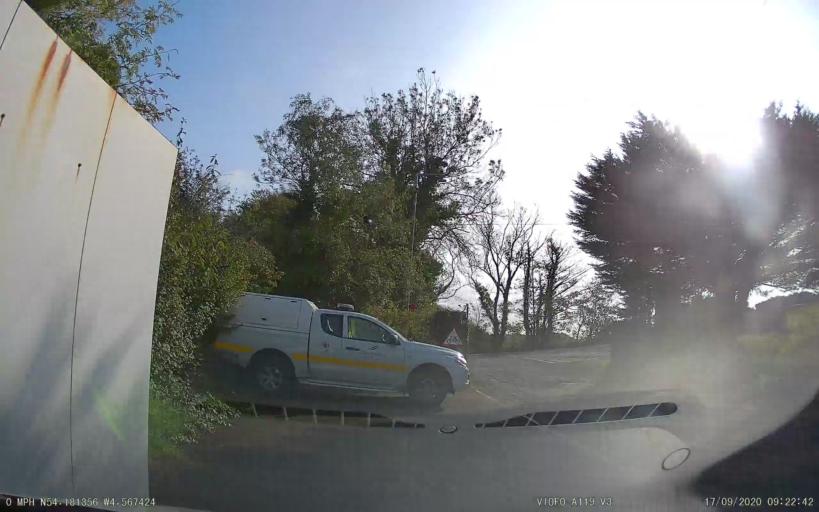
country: GB
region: Scotland
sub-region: Dumfries and Galloway
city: Newton Stewart
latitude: 54.7181
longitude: -4.5674
